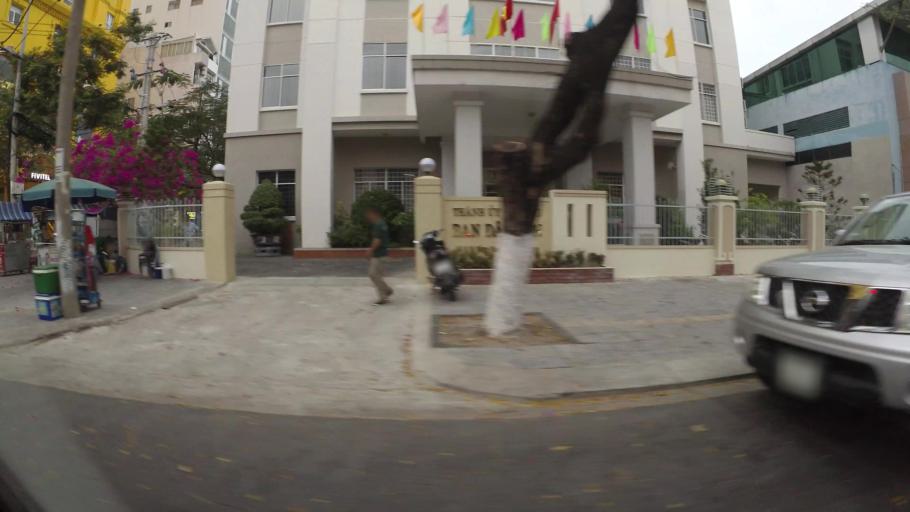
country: VN
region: Da Nang
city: Da Nang
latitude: 16.0641
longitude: 108.2208
